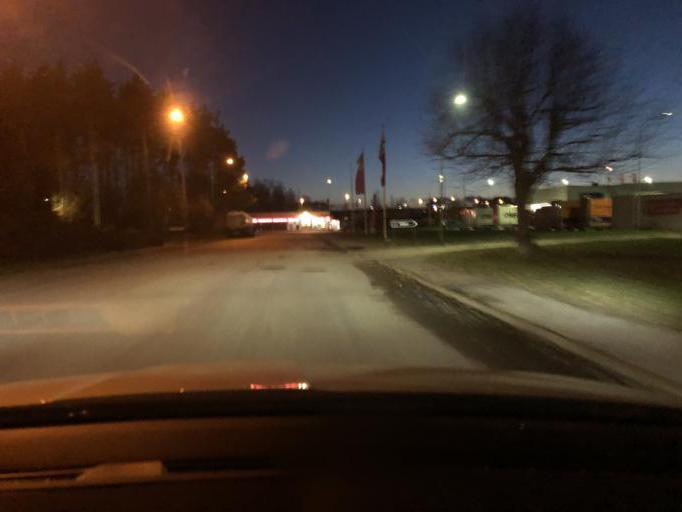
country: SE
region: Soedermanland
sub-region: Katrineholms Kommun
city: Katrineholm
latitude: 58.9986
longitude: 16.2230
